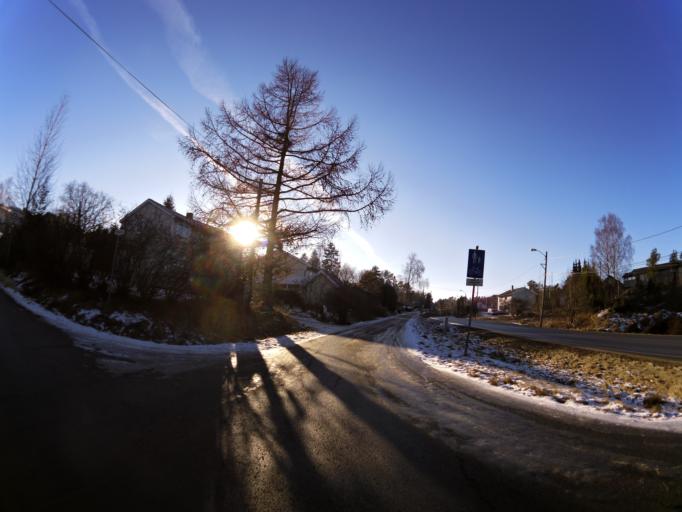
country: NO
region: Ostfold
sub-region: Fredrikstad
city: Fredrikstad
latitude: 59.2022
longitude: 10.8763
